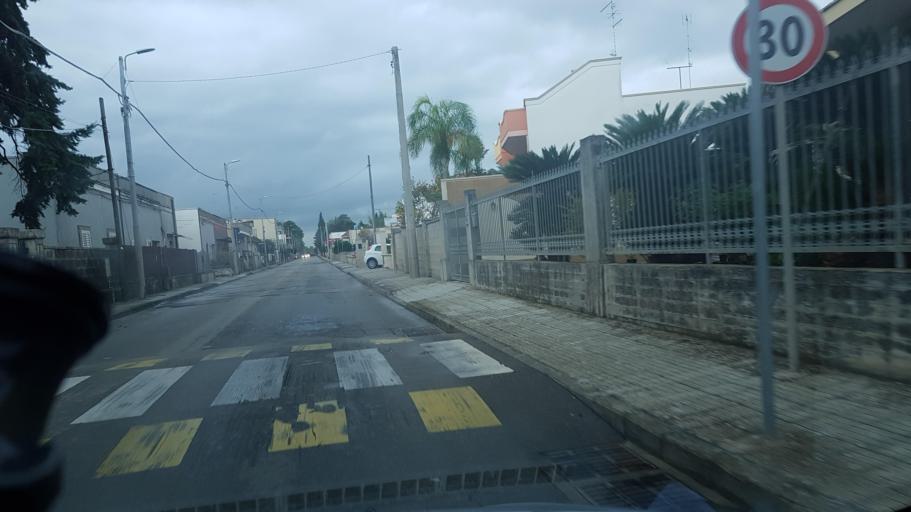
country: IT
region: Apulia
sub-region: Provincia di Lecce
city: Arnesano
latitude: 40.3640
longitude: 18.0789
